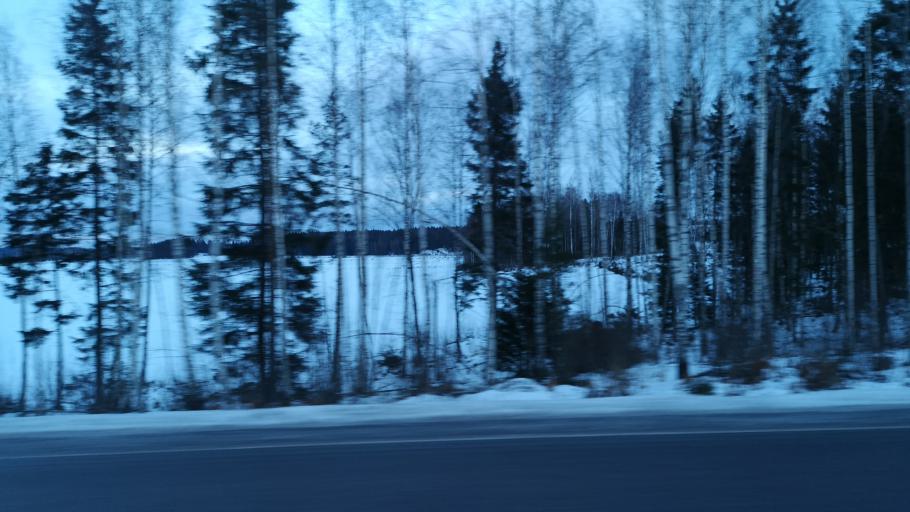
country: FI
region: Uusimaa
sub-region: Raaseporin
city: Inga
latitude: 60.0803
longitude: 23.9494
